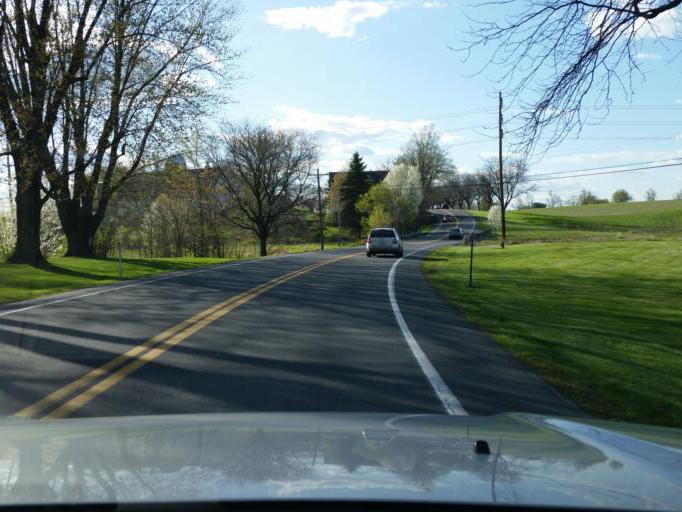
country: US
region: Pennsylvania
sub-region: Dauphin County
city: Hershey
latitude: 40.2565
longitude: -76.6339
